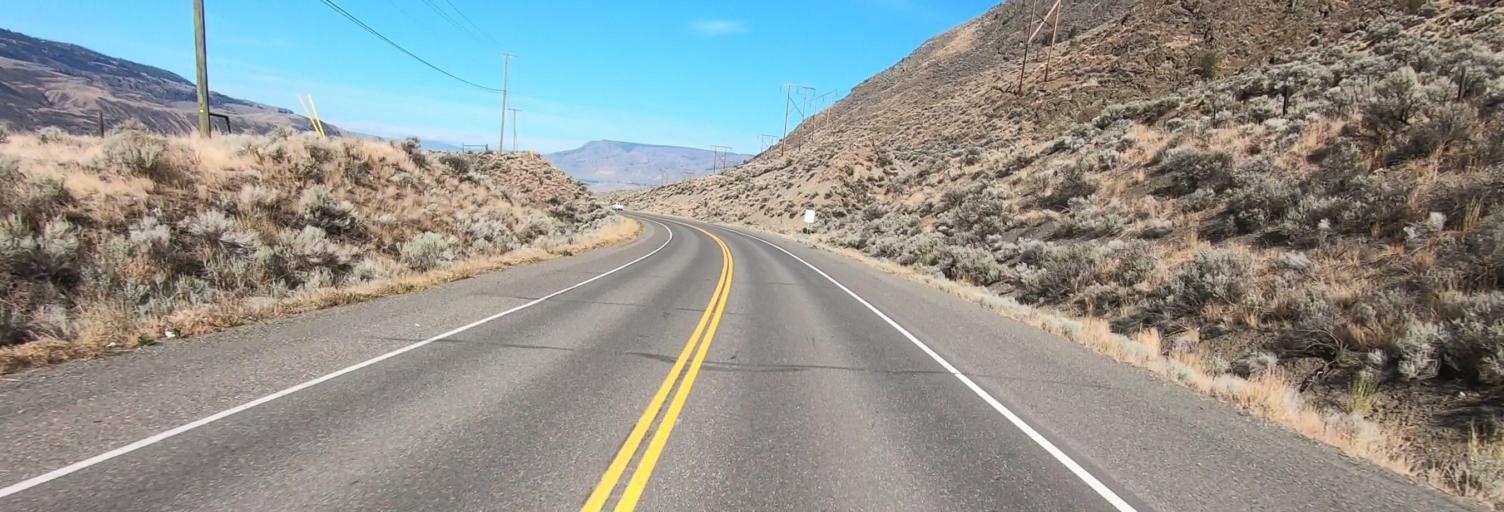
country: CA
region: British Columbia
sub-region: Thompson-Nicola Regional District
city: Ashcroft
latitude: 50.7689
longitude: -121.0102
